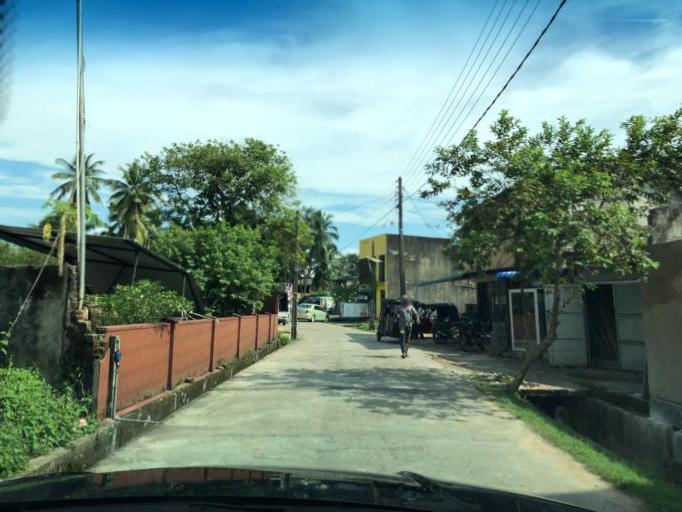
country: LK
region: Western
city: Horana South
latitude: 6.7181
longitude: 80.0602
